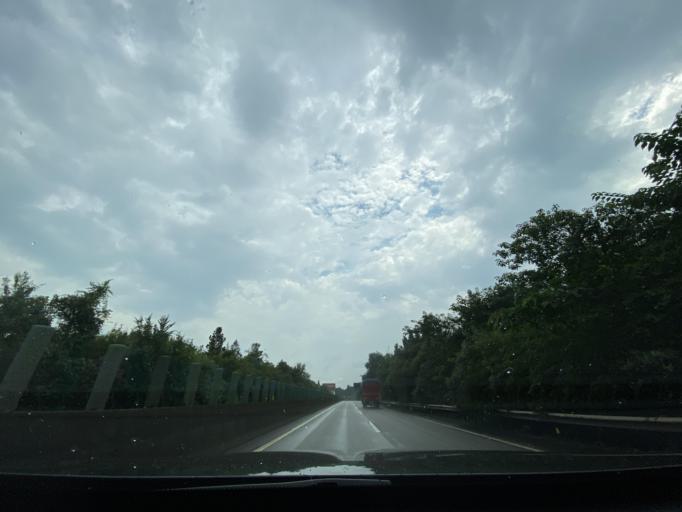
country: CN
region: Sichuan
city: Yanjiang
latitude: 30.0647
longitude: 104.5980
